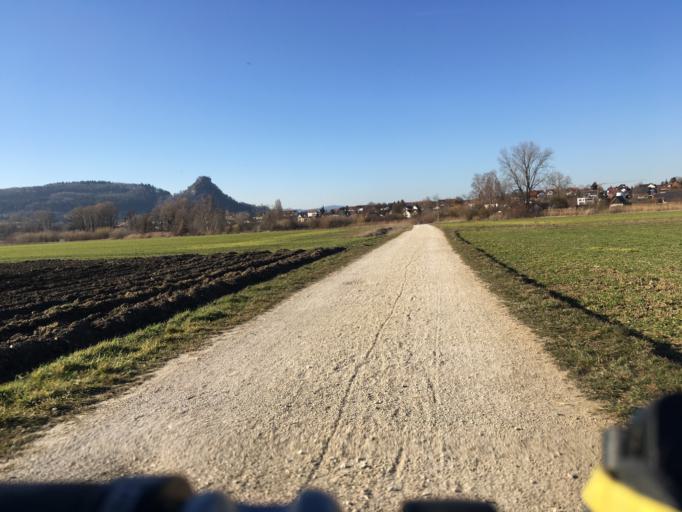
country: DE
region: Baden-Wuerttemberg
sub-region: Freiburg Region
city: Singen
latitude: 47.7868
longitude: 8.8456
